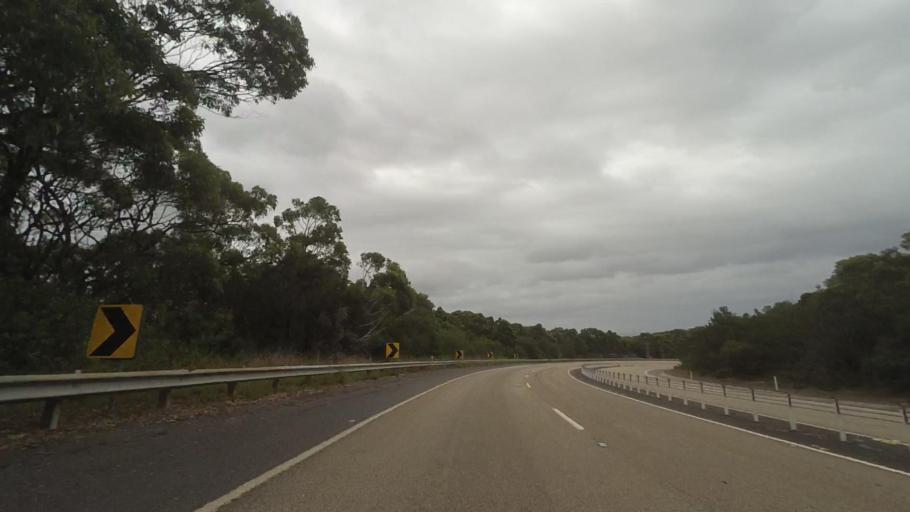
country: AU
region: New South Wales
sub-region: Lake Macquarie Shire
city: Arcadia vale
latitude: -33.1305
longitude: 151.6284
